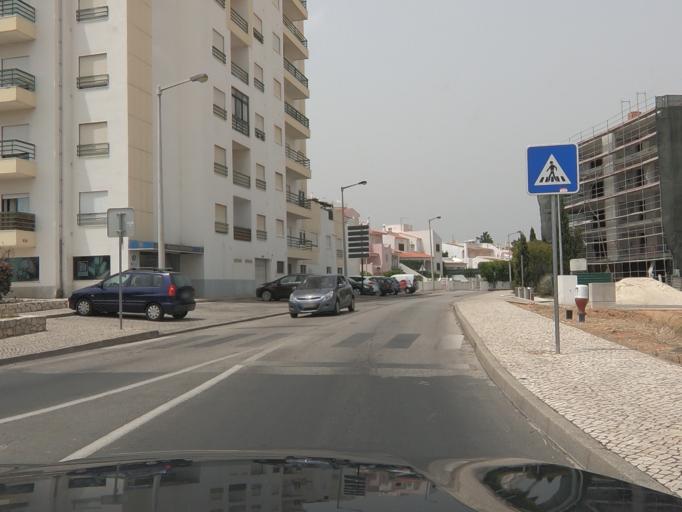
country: PT
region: Faro
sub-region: Portimao
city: Portimao
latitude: 37.1272
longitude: -8.5427
